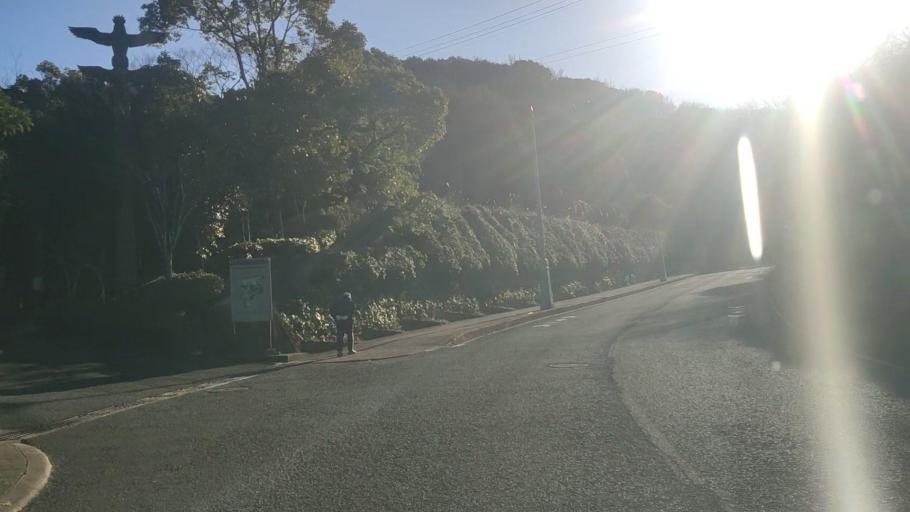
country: JP
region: Oita
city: Oita
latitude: 33.2264
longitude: 131.6022
